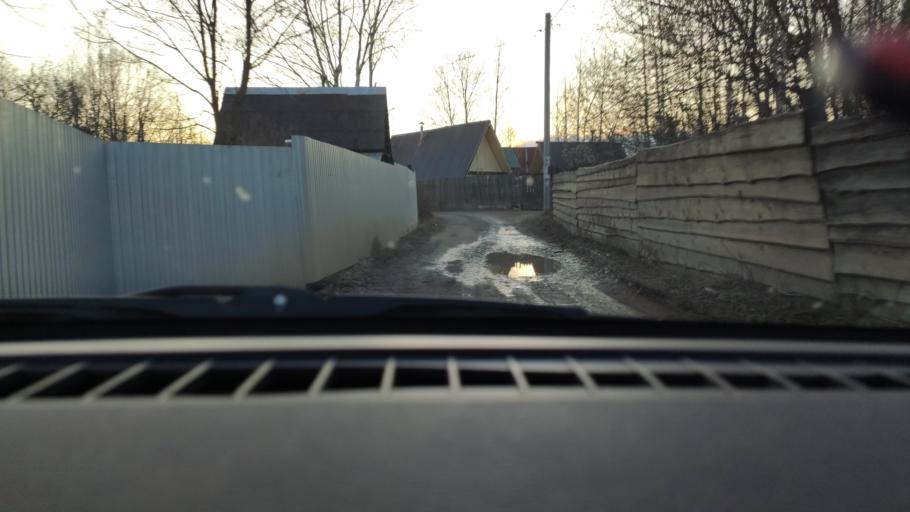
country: RU
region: Perm
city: Perm
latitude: 58.0825
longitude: 56.3179
